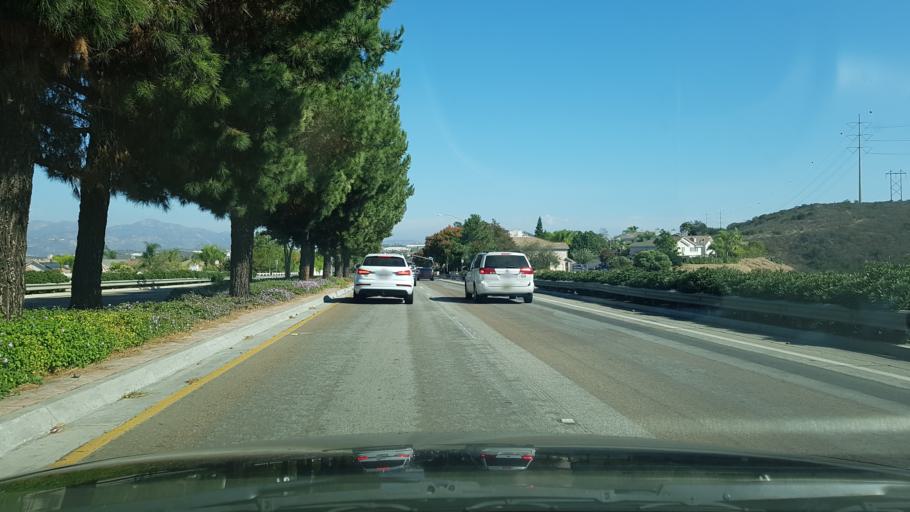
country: US
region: California
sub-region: San Diego County
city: Poway
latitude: 32.9342
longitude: -117.0808
